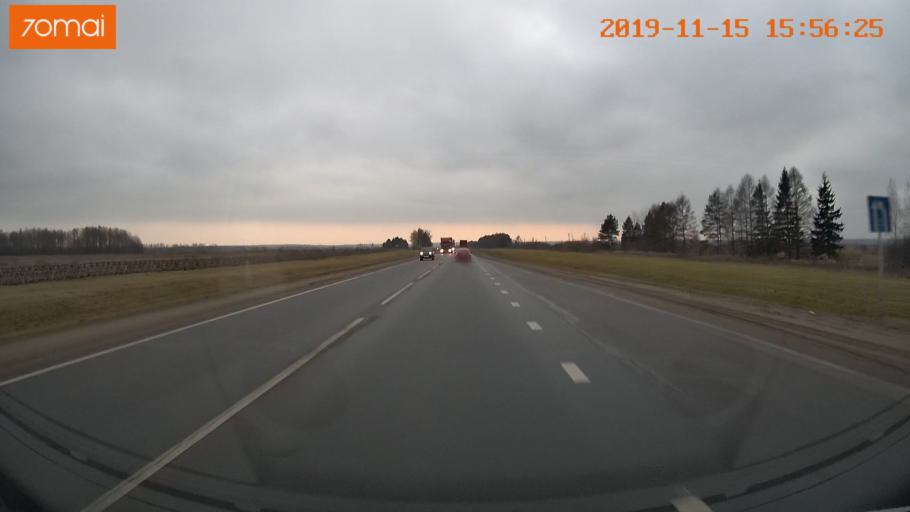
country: RU
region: Jaroslavl
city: Yaroslavl
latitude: 57.8423
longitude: 39.9738
